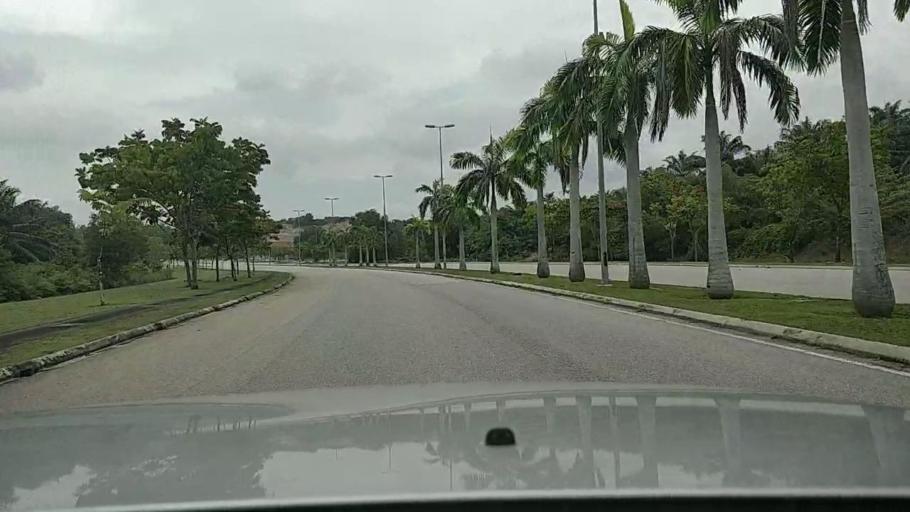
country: MY
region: Putrajaya
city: Putrajaya
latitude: 2.8993
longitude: 101.6465
